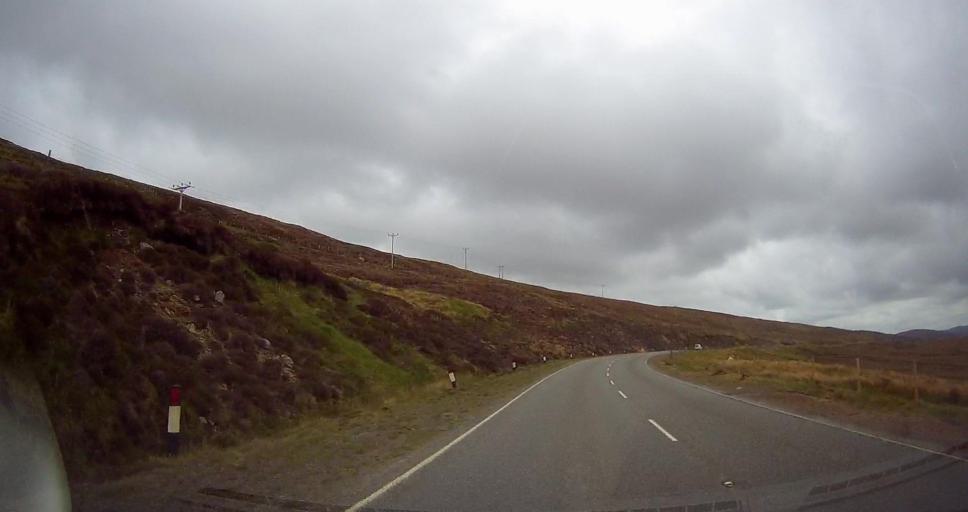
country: GB
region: Scotland
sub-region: Shetland Islands
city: Lerwick
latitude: 60.3060
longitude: -1.2411
